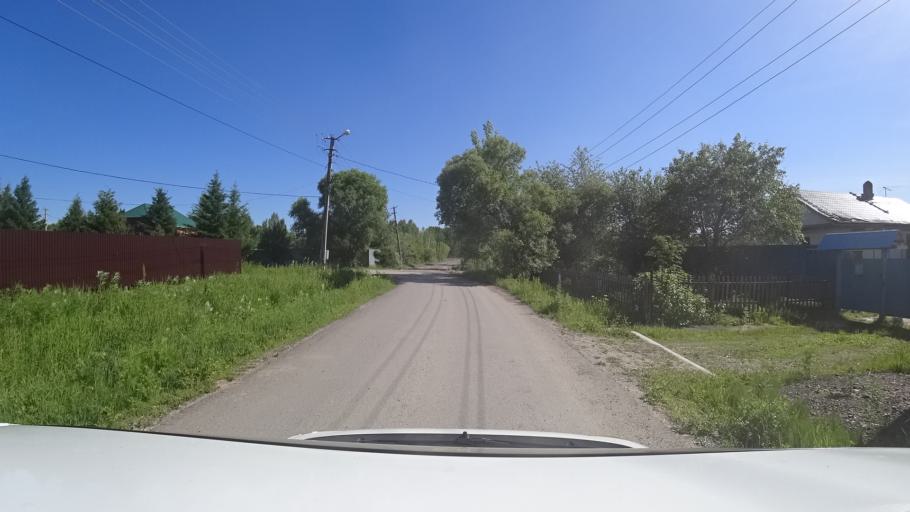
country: RU
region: Khabarovsk Krai
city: Topolevo
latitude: 48.5506
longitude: 135.1691
